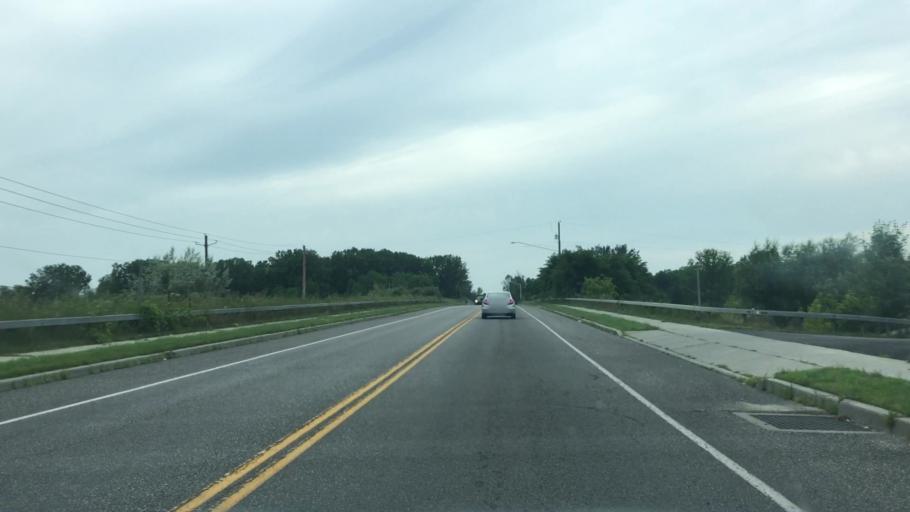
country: US
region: New York
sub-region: Clinton County
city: Plattsburgh West
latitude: 44.6870
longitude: -73.4889
